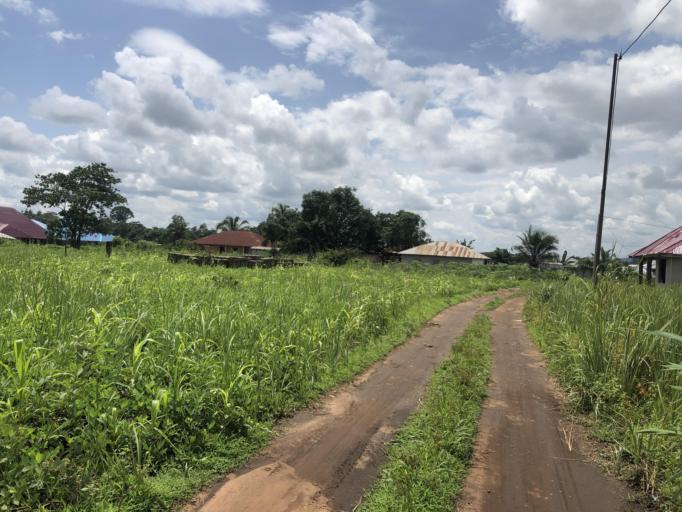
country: SL
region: Northern Province
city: Magburaka
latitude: 8.7058
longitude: -11.9241
